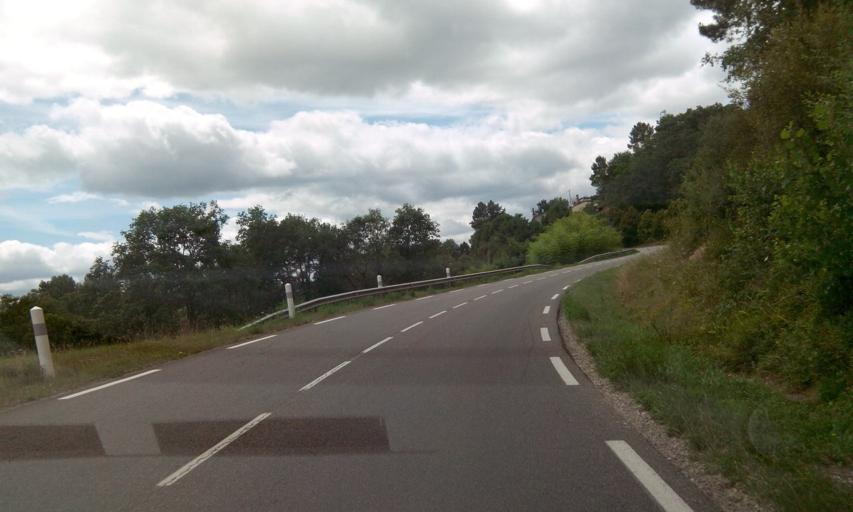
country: FR
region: Limousin
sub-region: Departement de la Correze
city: Brive-la-Gaillarde
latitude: 45.1300
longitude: 1.5546
